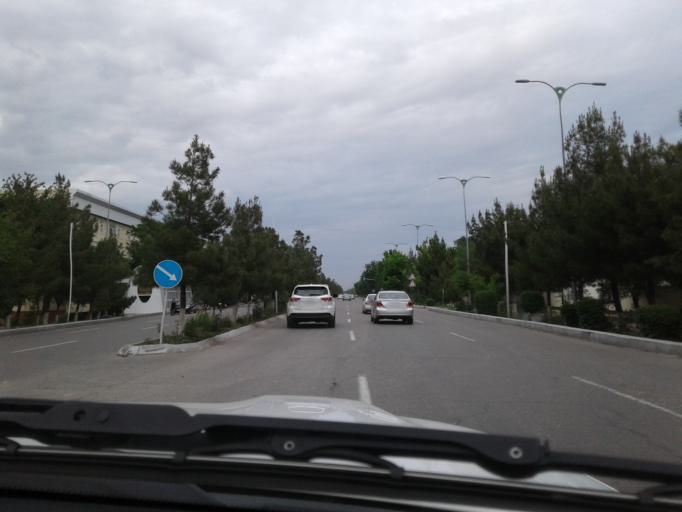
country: TM
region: Mary
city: Mary
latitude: 37.5860
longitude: 61.8615
